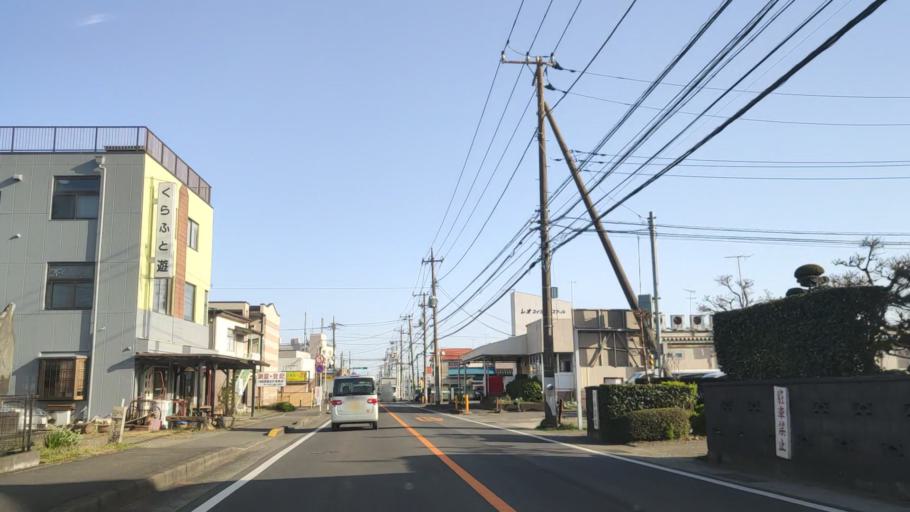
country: JP
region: Kanagawa
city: Zama
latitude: 35.5190
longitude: 139.3316
